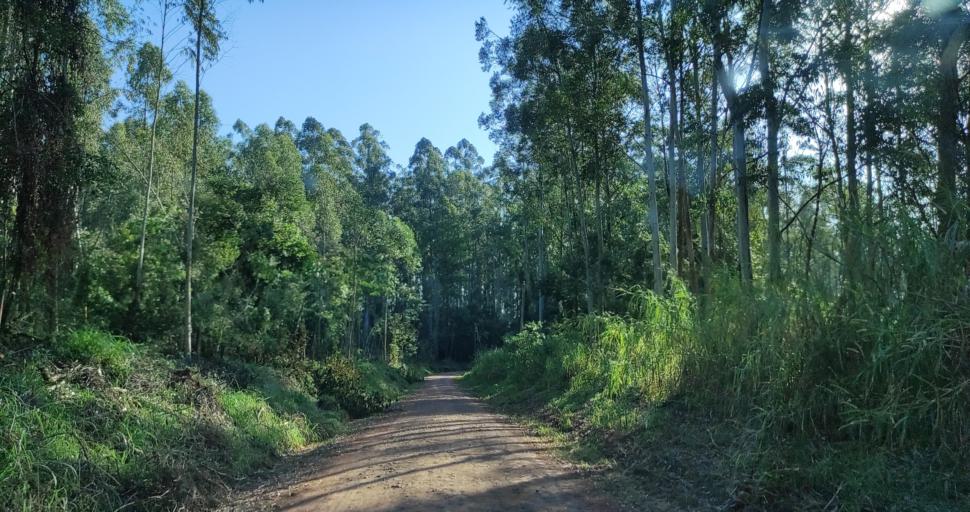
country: AR
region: Misiones
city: Capiovi
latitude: -26.8663
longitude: -55.1308
